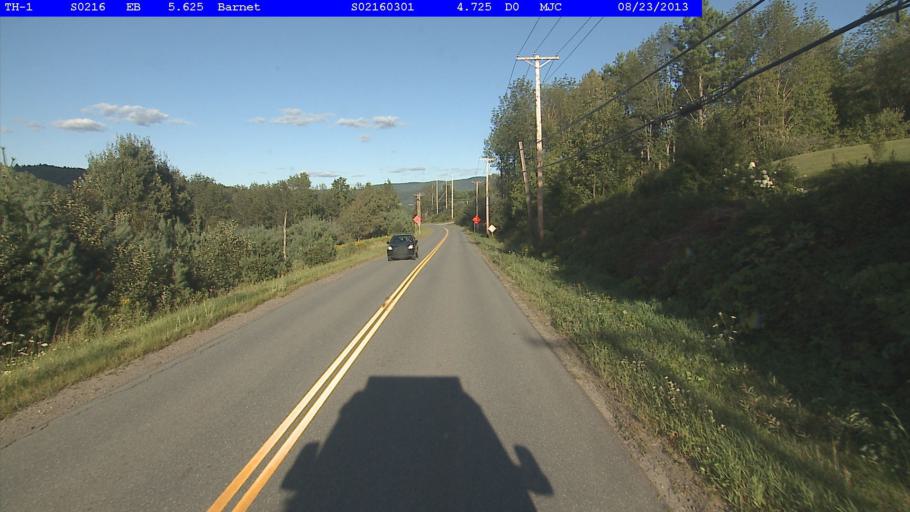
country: US
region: Vermont
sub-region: Caledonia County
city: Saint Johnsbury
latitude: 44.3004
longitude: -72.0662
